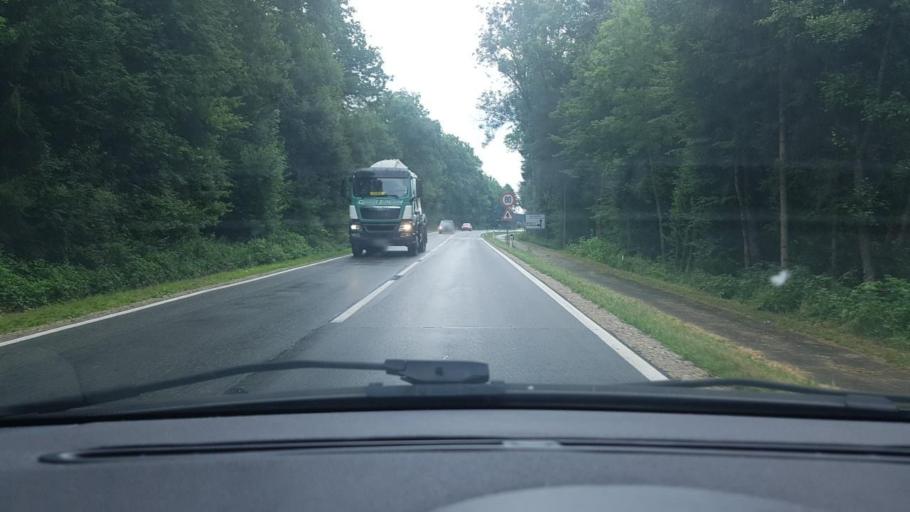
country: AT
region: Styria
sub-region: Politischer Bezirk Suedoststeiermark
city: Weinburg am Sassbach
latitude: 46.7537
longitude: 15.7007
